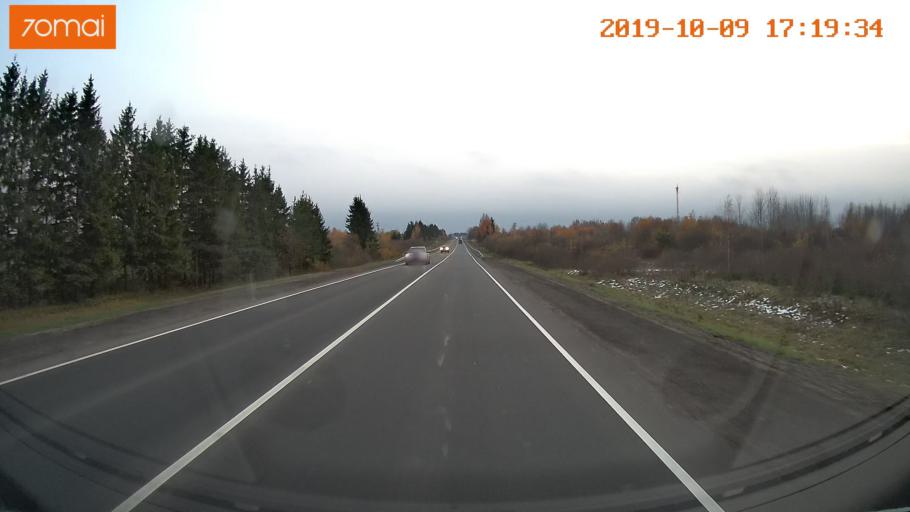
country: RU
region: Ivanovo
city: Furmanov
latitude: 57.2446
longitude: 41.1514
